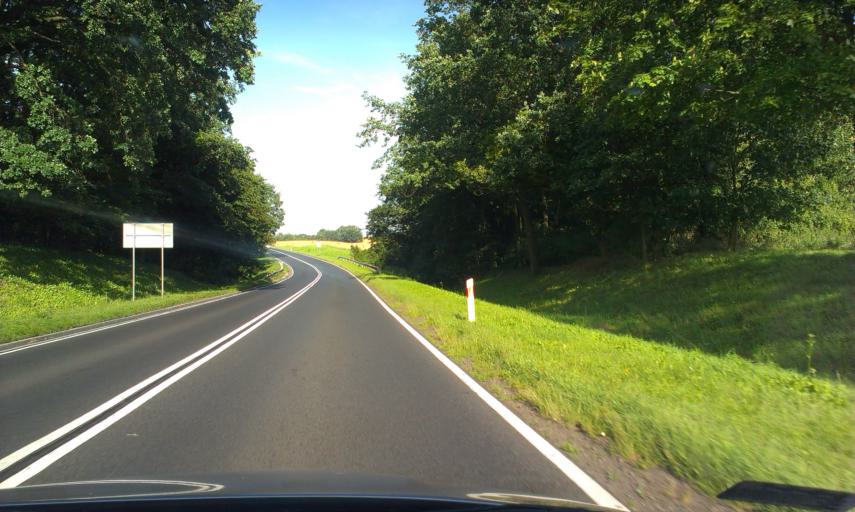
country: PL
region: Kujawsko-Pomorskie
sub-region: Powiat nakielski
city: Slesin
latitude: 53.1673
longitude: 17.7542
